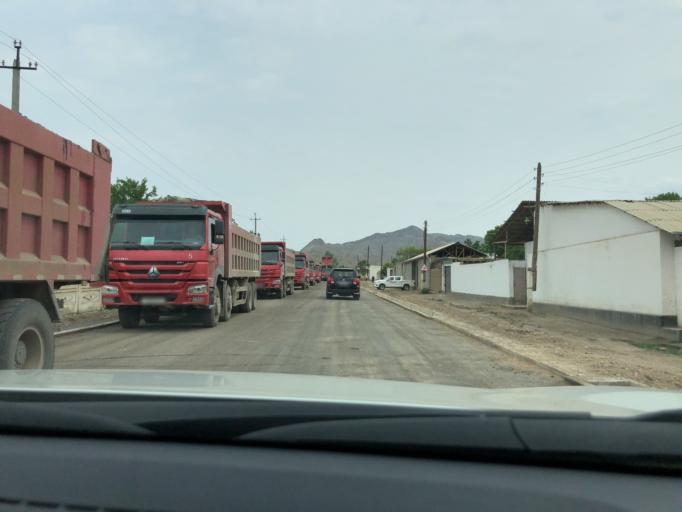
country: TJ
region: Viloyati Sughd
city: Isfara
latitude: 40.1576
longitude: 70.6303
